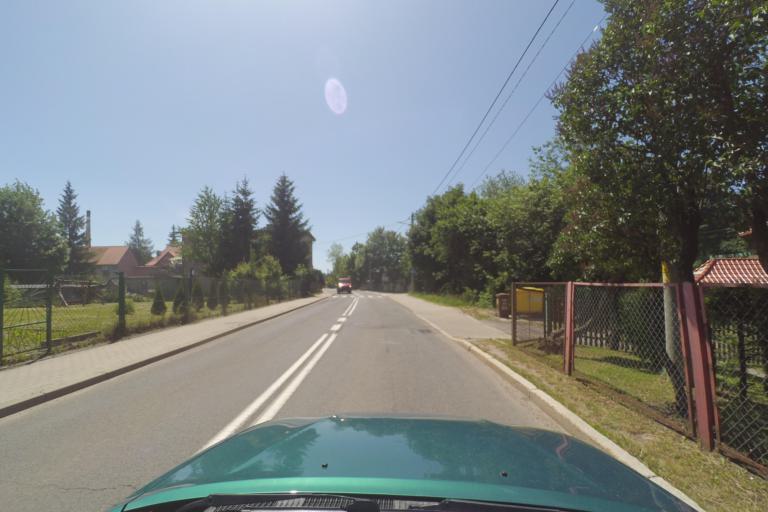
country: PL
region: Lower Silesian Voivodeship
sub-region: Powiat walbrzyski
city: Mieroszow
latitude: 50.6685
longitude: 16.1889
